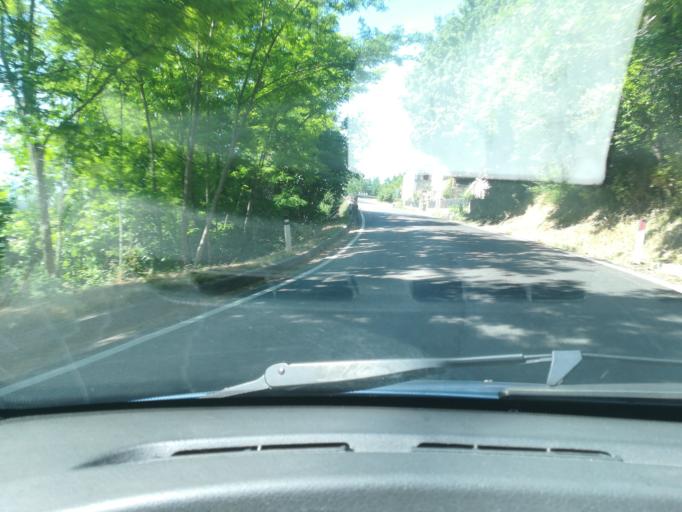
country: IT
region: The Marches
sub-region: Provincia di Macerata
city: San Ginesio
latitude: 43.1061
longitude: 13.3274
